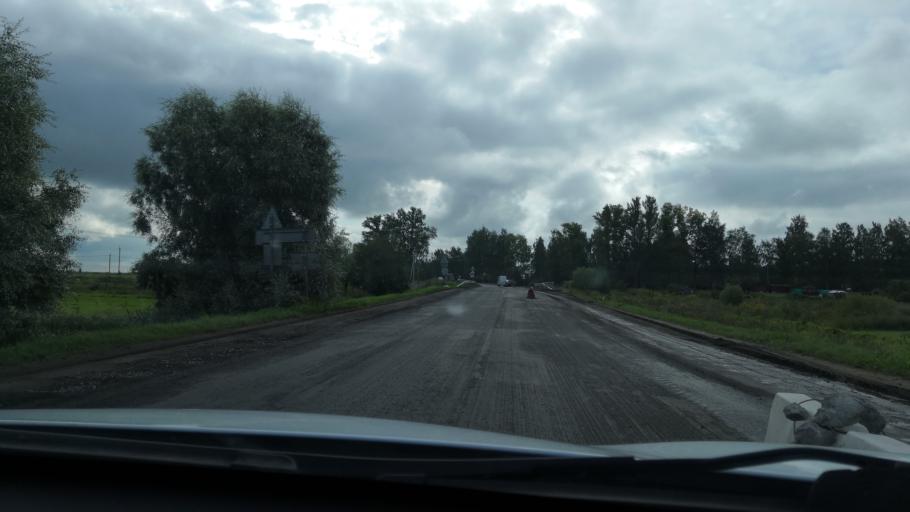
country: RU
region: St.-Petersburg
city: Tyarlevo
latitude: 59.7116
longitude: 30.4669
